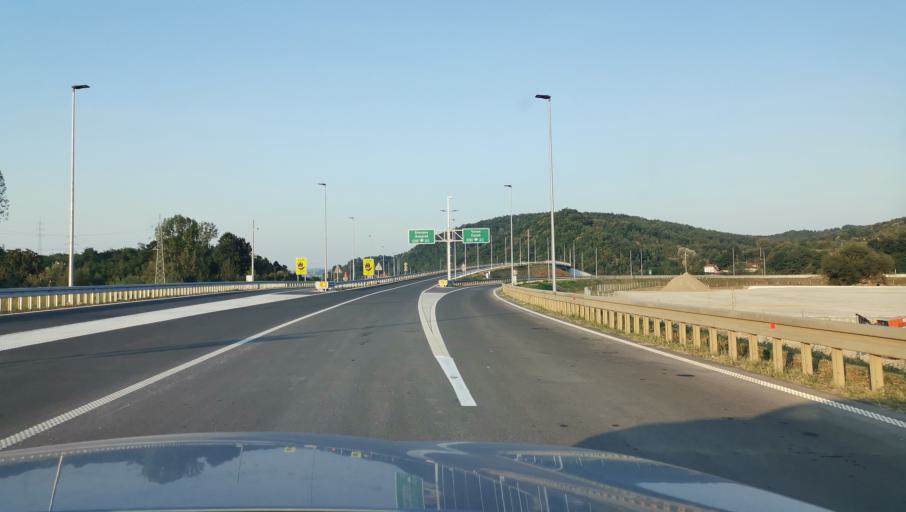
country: RS
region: Central Serbia
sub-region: Kolubarski Okrug
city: Ljig
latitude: 44.2322
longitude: 20.2505
